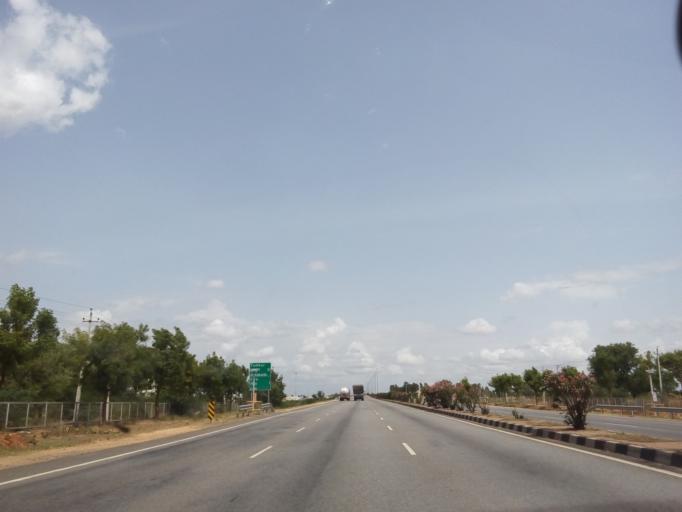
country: IN
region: Karnataka
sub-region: Tumkur
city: Sira
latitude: 13.7416
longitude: 76.8898
